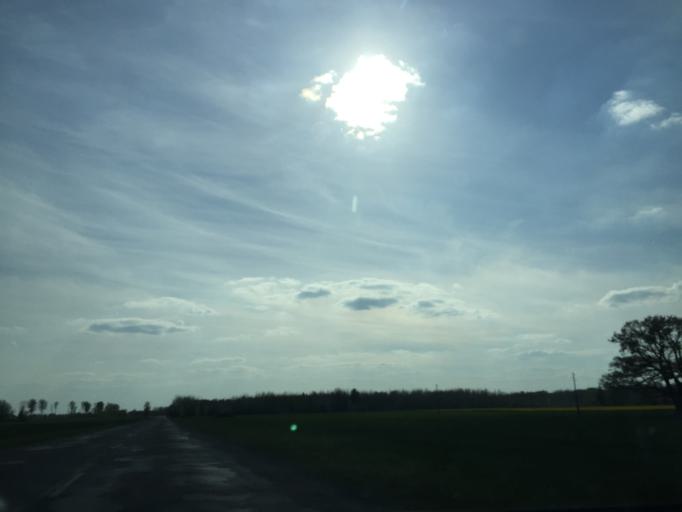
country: LV
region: Bauskas Rajons
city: Bauska
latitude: 56.4632
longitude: 24.2831
